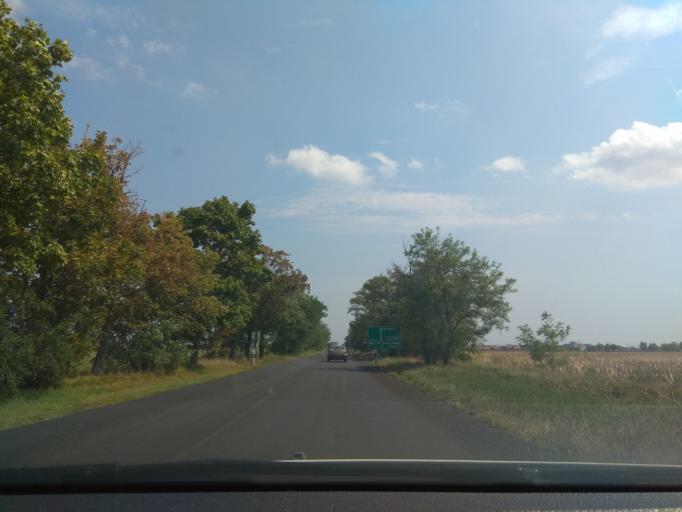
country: HU
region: Borsod-Abauj-Zemplen
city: Mezokovesd
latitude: 47.8115
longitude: 20.5381
